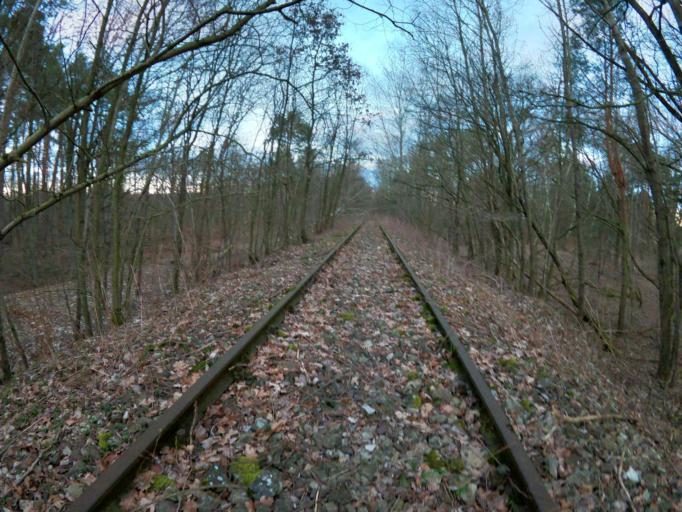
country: PL
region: West Pomeranian Voivodeship
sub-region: Powiat kamienski
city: Golczewo
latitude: 53.8298
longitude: 14.9502
